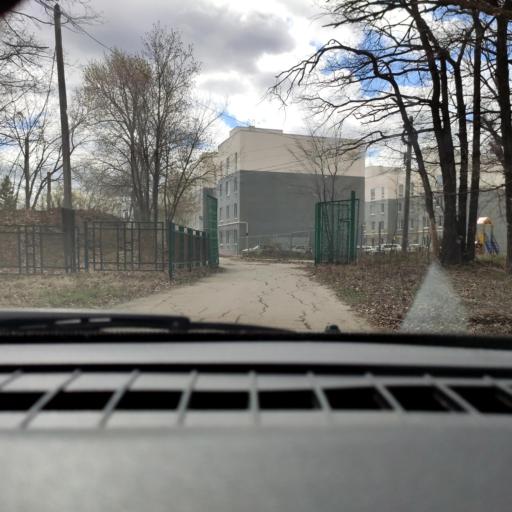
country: RU
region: Samara
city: Volzhskiy
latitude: 53.3532
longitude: 50.2053
